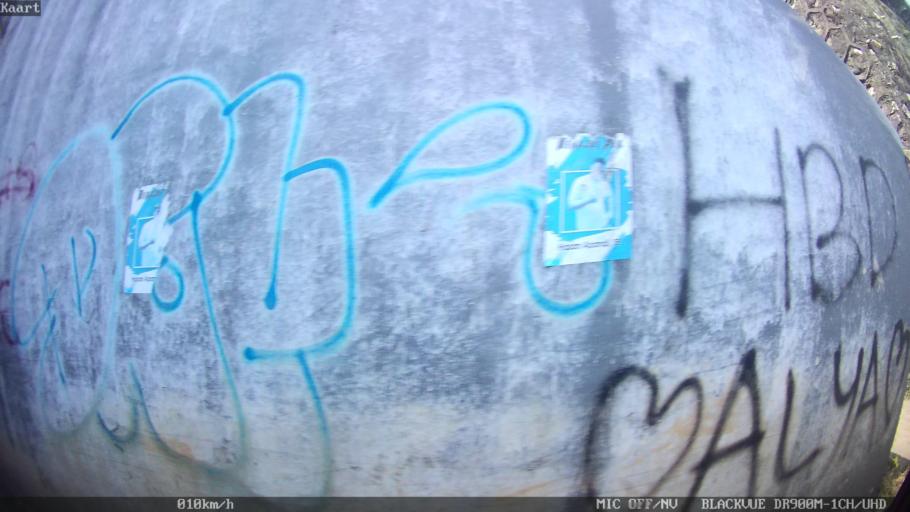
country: ID
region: Lampung
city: Kedaton
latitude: -5.4036
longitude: 105.2609
